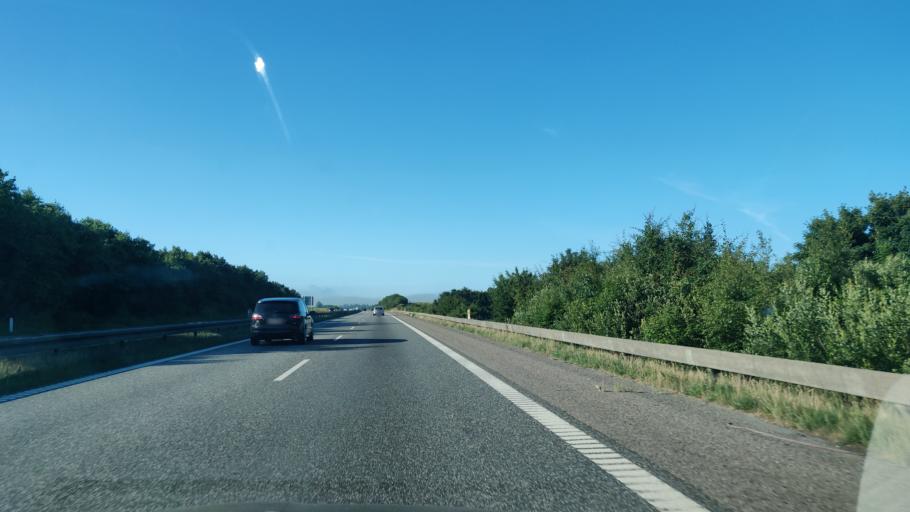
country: DK
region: North Denmark
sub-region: Mariagerfjord Kommune
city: Hobro
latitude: 56.7656
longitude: 9.6937
